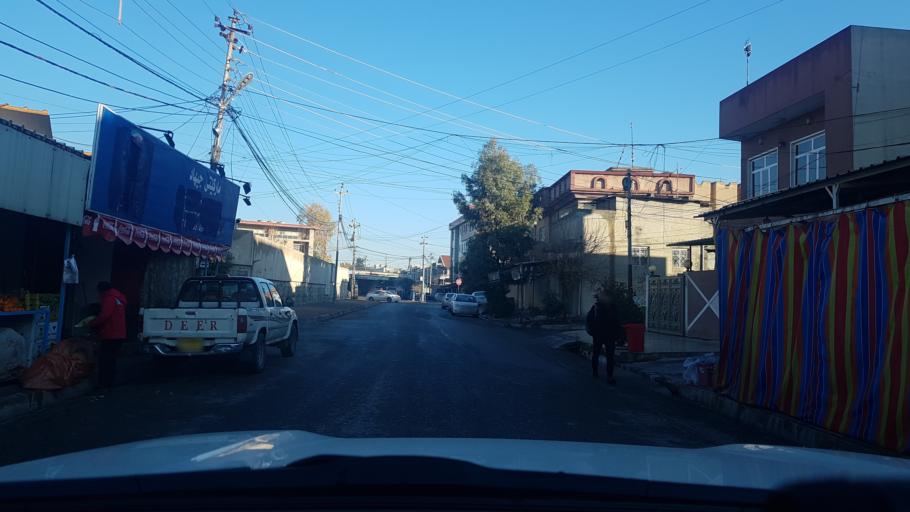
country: IQ
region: Arbil
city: Erbil
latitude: 36.2058
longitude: 44.0087
